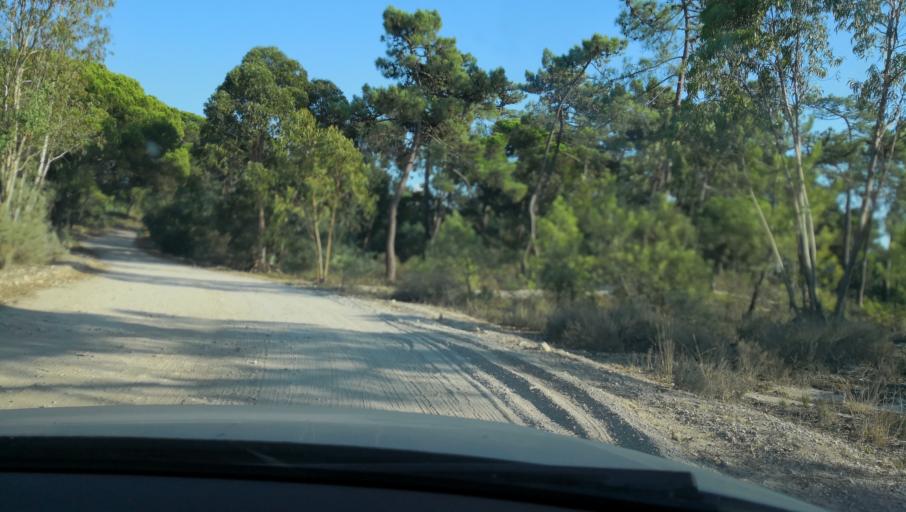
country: PT
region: Setubal
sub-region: Setubal
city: Setubal
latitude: 38.4687
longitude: -8.8752
